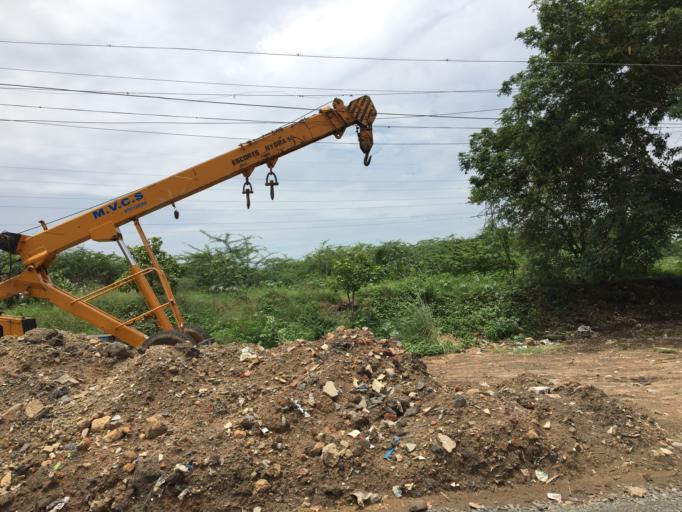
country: IN
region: Tamil Nadu
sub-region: Kancheepuram
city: Madipakkam
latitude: 12.9600
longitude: 80.2147
